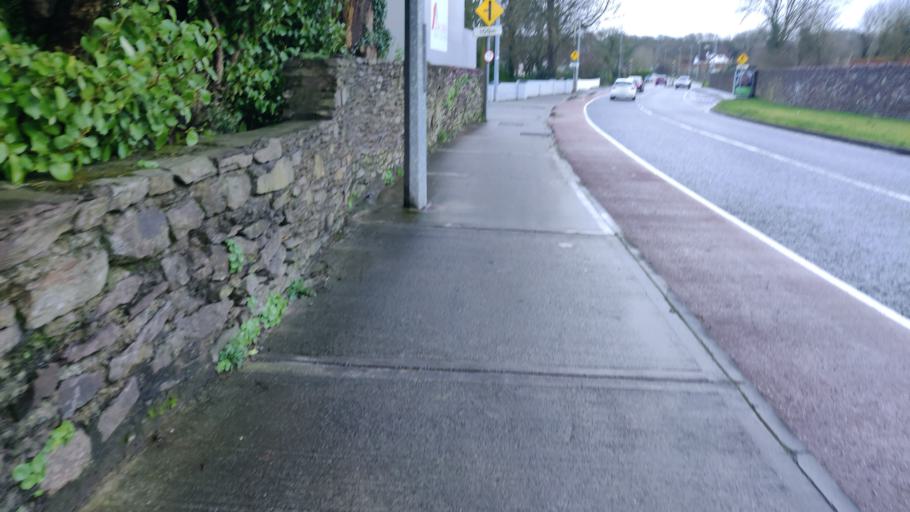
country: IE
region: Munster
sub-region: County Cork
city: Cork
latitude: 51.8703
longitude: -8.4180
